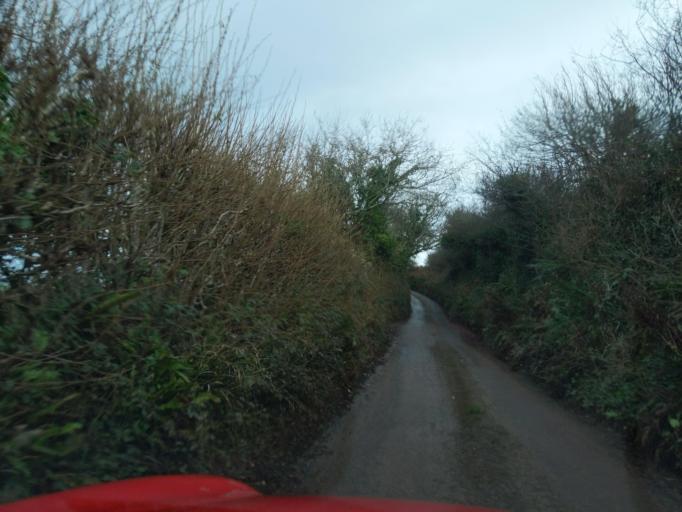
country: GB
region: England
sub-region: Devon
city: Salcombe
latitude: 50.2513
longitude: -3.6700
